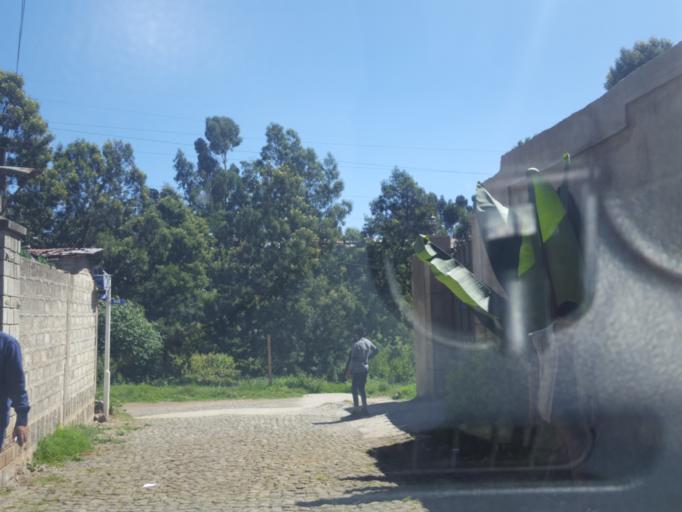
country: ET
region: Adis Abeba
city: Addis Ababa
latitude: 9.0596
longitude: 38.7459
